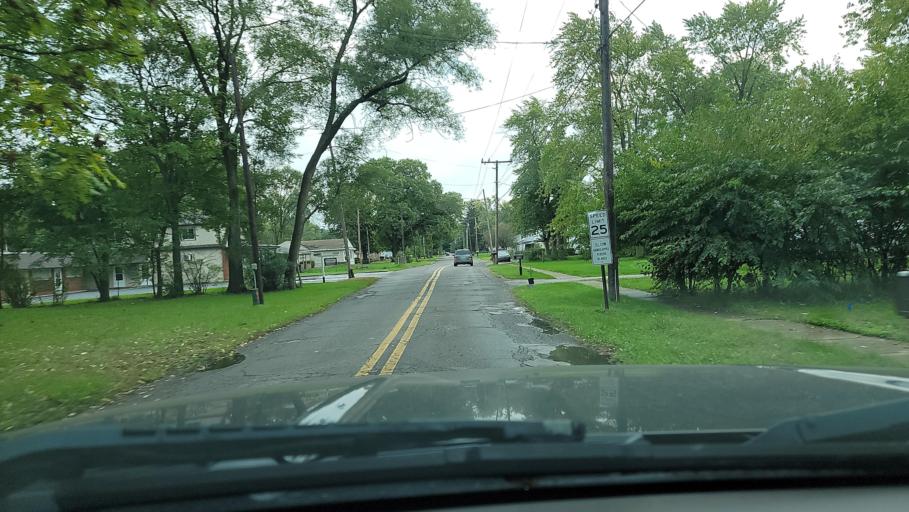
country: US
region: Indiana
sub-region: Lake County
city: Lake Station
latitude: 41.5703
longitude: -87.2170
